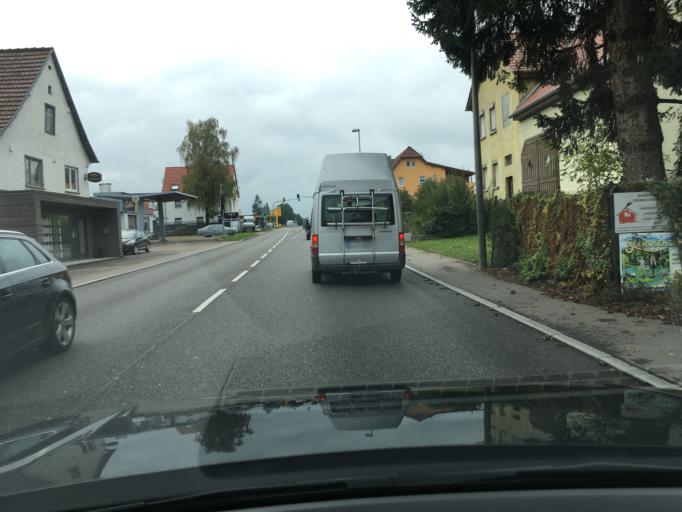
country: DE
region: Baden-Wuerttemberg
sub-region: Tuebingen Region
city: Ofterdingen
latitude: 48.4183
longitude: 9.0376
